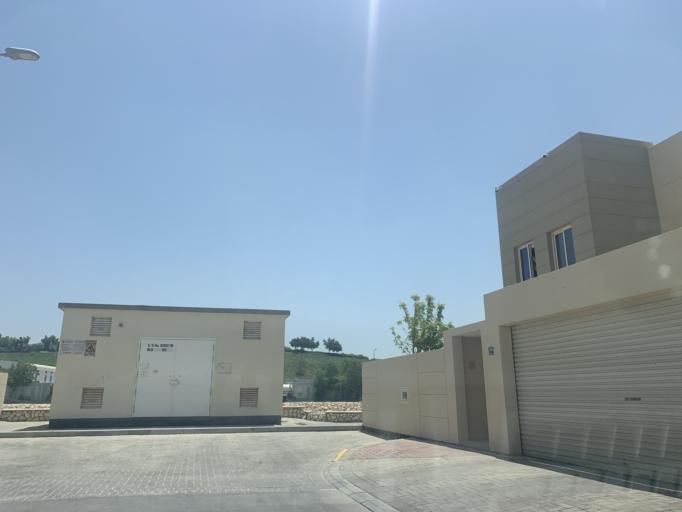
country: BH
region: Manama
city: Jidd Hafs
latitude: 26.2383
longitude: 50.4707
